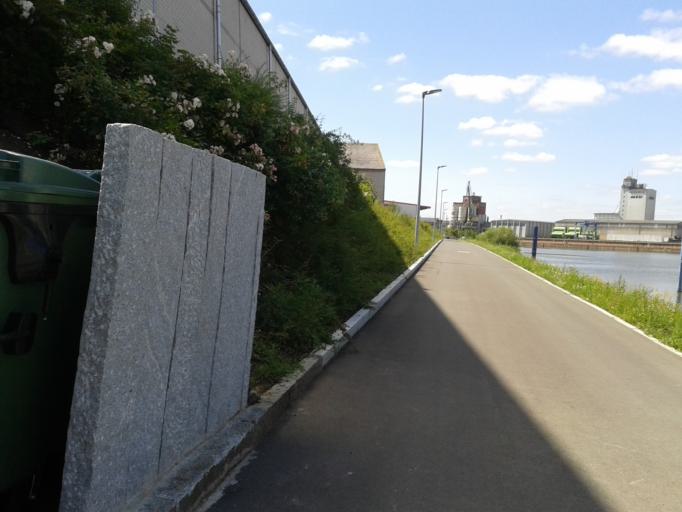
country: DE
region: Bavaria
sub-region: Upper Franconia
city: Hallstadt
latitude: 49.9065
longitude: 10.8723
